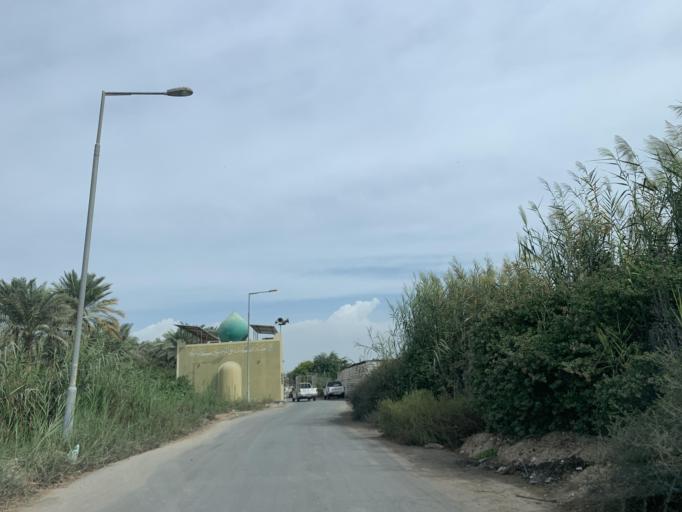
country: BH
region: Central Governorate
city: Madinat Hamad
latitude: 26.1134
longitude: 50.4757
